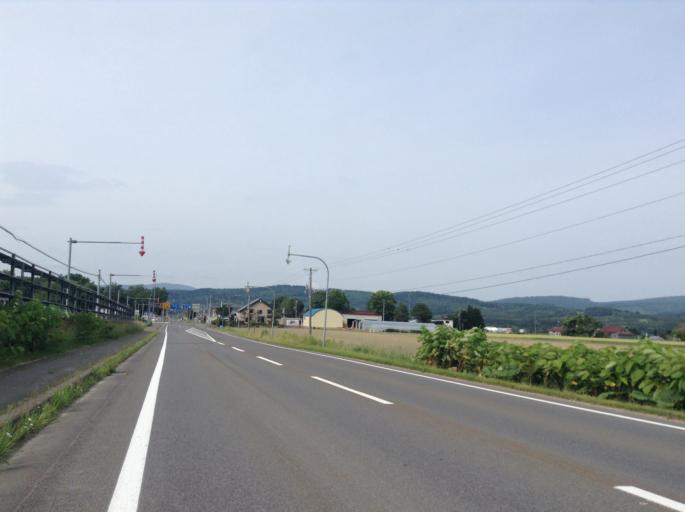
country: JP
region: Hokkaido
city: Nayoro
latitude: 44.4346
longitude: 142.4025
